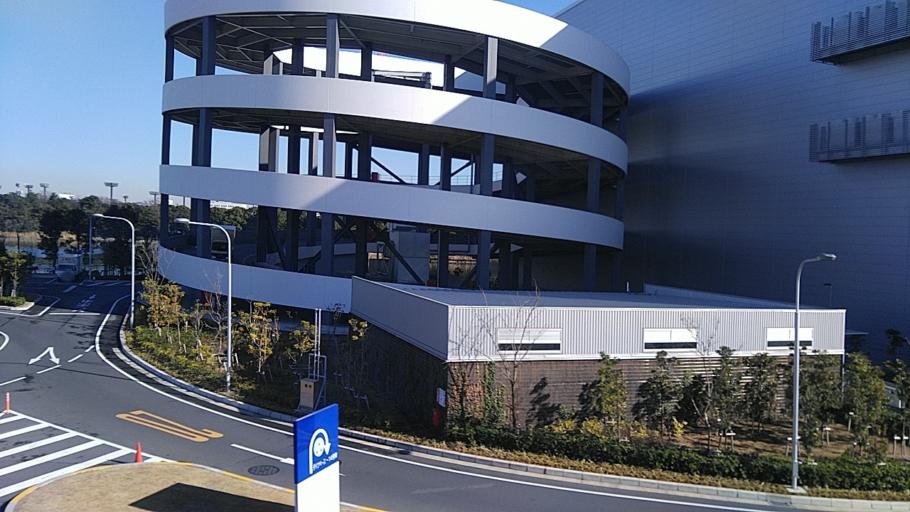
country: JP
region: Kanagawa
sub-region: Kawasaki-shi
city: Kawasaki
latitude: 35.5885
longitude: 139.7464
